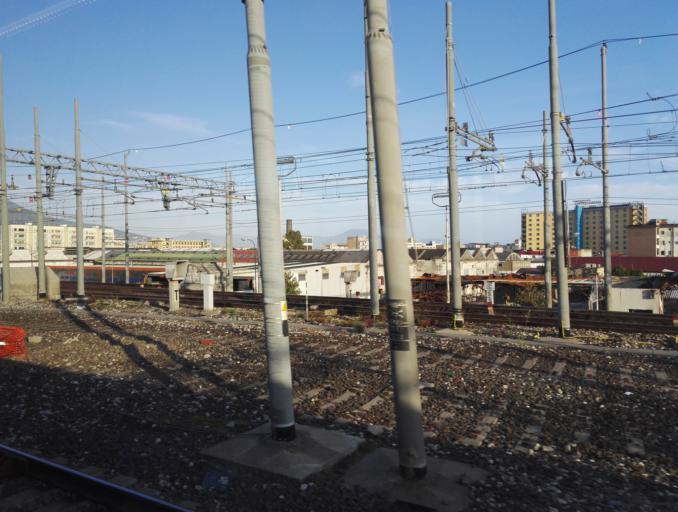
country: IT
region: Campania
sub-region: Provincia di Napoli
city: Napoli
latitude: 40.8538
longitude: 14.2851
